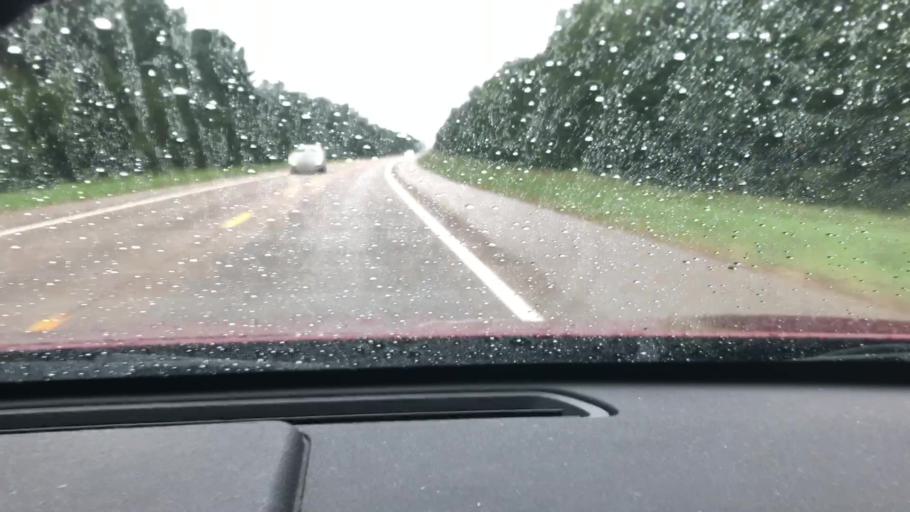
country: US
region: Arkansas
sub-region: Columbia County
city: Magnolia
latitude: 33.2992
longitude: -93.2644
